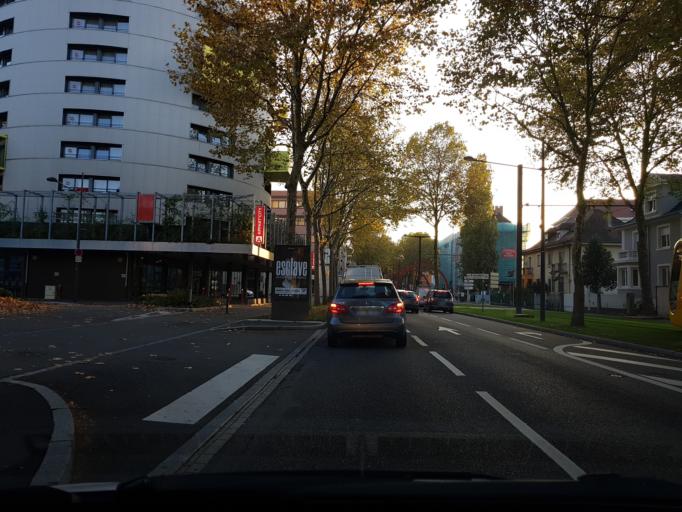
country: FR
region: Alsace
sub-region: Departement du Haut-Rhin
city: Mulhouse
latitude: 47.7573
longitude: 7.3492
